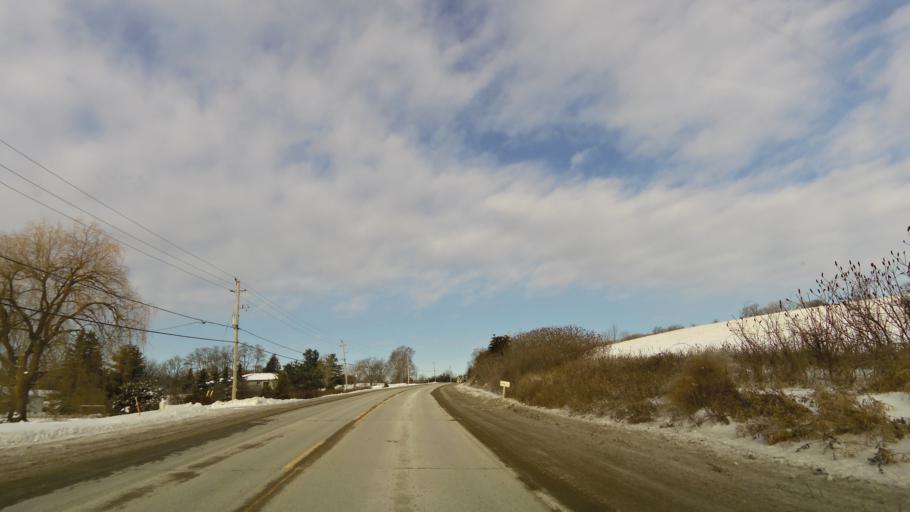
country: CA
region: Ontario
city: Quinte West
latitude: 44.0812
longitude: -77.7737
